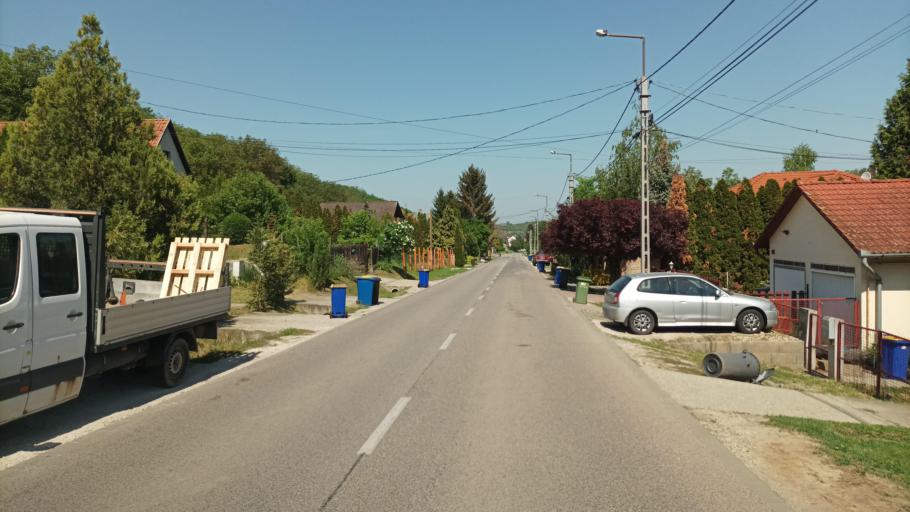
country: HU
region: Pest
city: Suelysap
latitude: 47.4428
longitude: 19.5293
